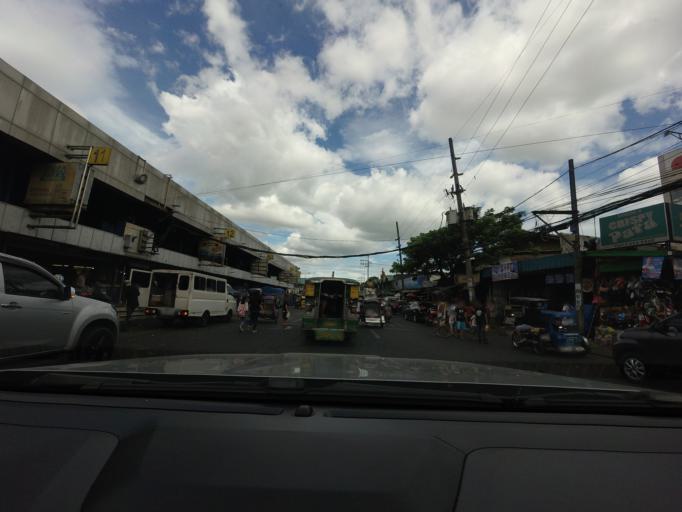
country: PH
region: Calabarzon
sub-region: Province of Rizal
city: Pateros
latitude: 14.5577
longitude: 121.0842
